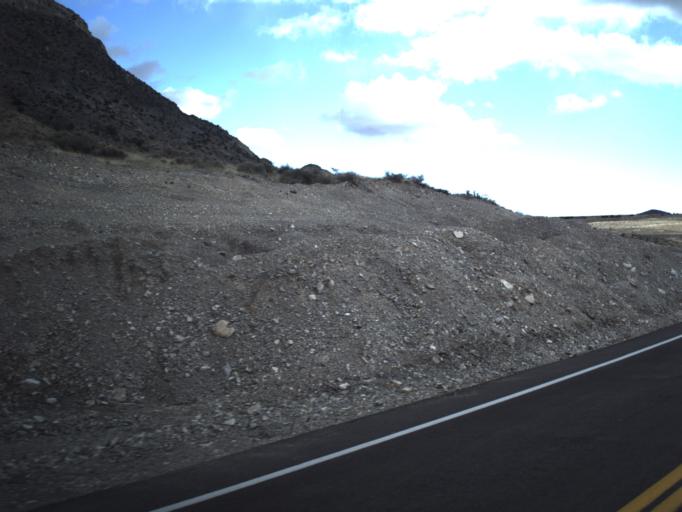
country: US
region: Utah
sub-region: Beaver County
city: Milford
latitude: 38.5054
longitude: -113.5976
